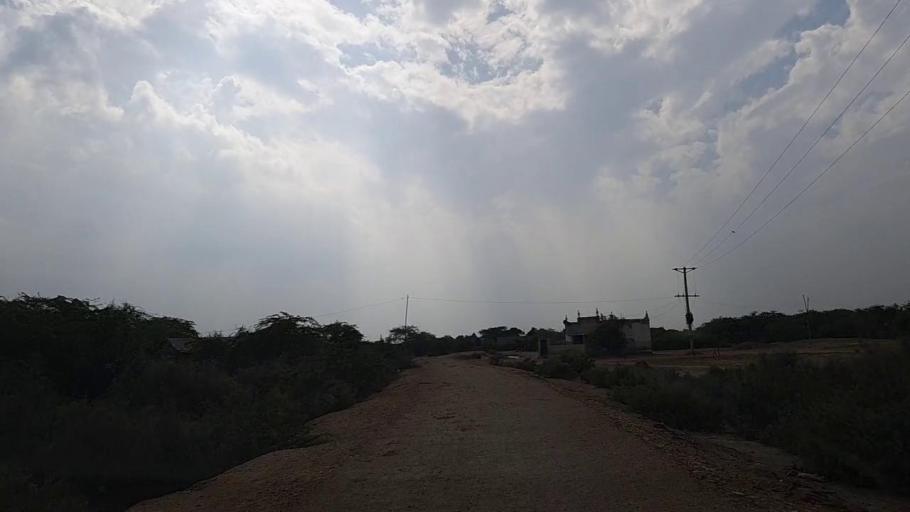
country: PK
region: Sindh
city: Daro Mehar
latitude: 24.7202
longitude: 68.1374
